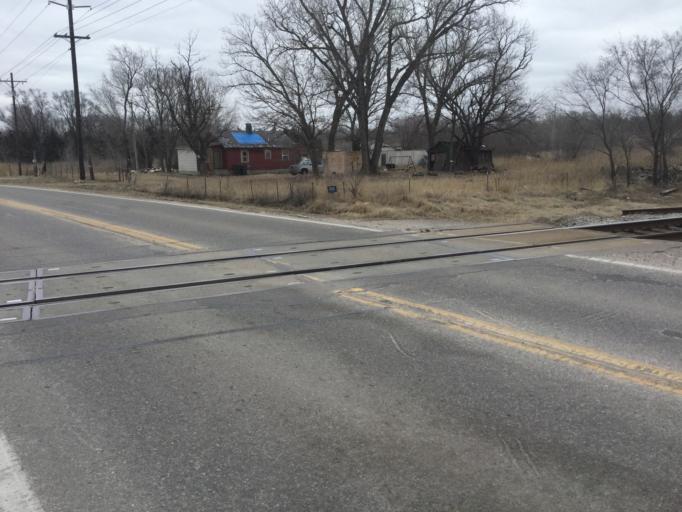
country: US
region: Kansas
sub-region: Sedgwick County
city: Haysville
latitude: 37.5935
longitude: -97.3440
